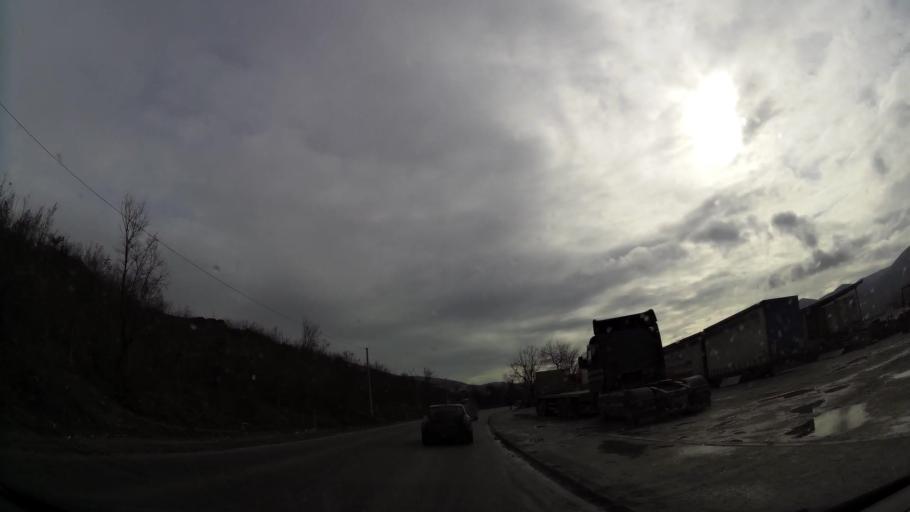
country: XK
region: Ferizaj
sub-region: Hani i Elezit
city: Hani i Elezit
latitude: 42.1551
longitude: 21.2956
